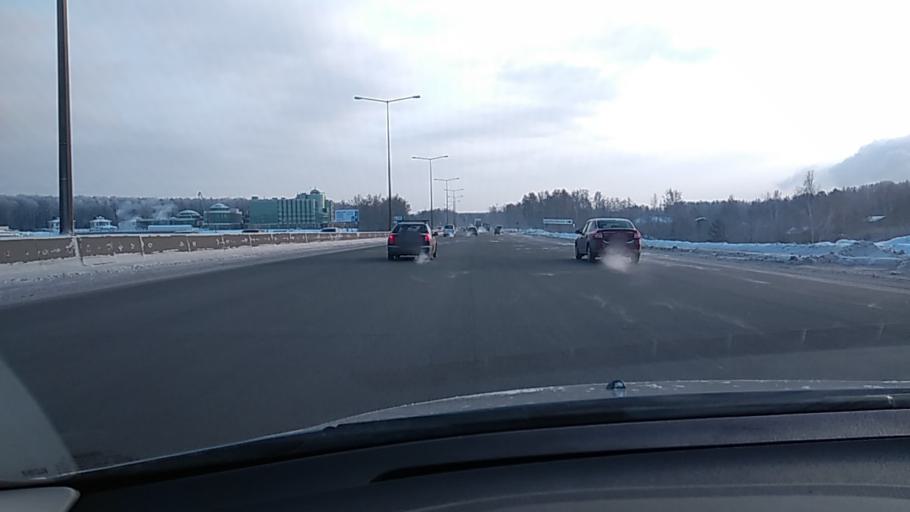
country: RU
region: Sverdlovsk
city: Istok
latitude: 56.7782
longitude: 60.7100
